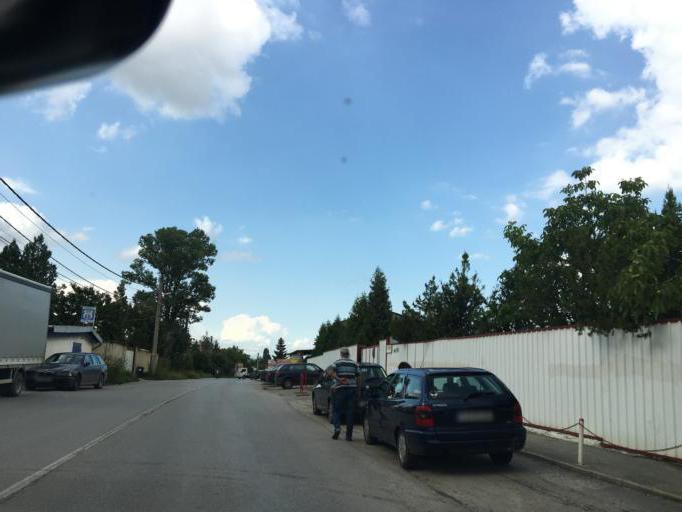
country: BG
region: Sofia-Capital
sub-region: Stolichna Obshtina
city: Sofia
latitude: 42.6411
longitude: 23.3531
